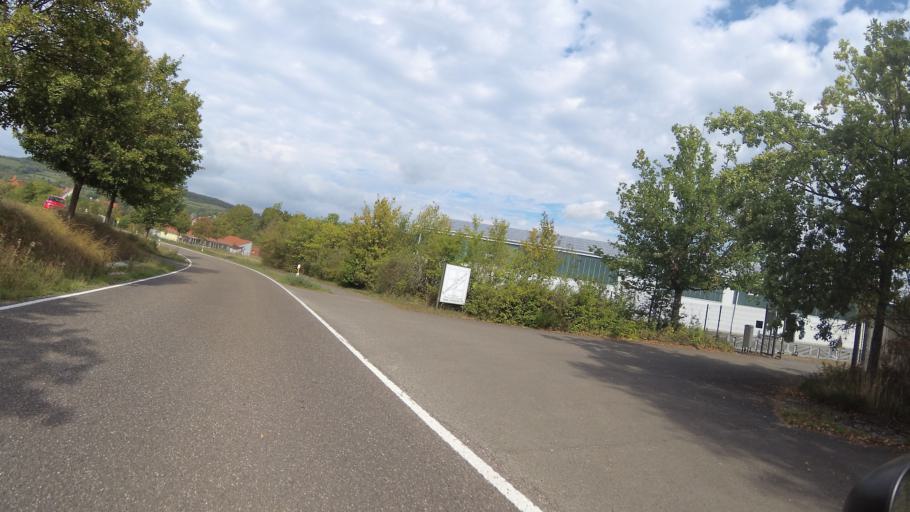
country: DE
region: Saarland
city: Gersheim
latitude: 49.1353
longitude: 7.1943
